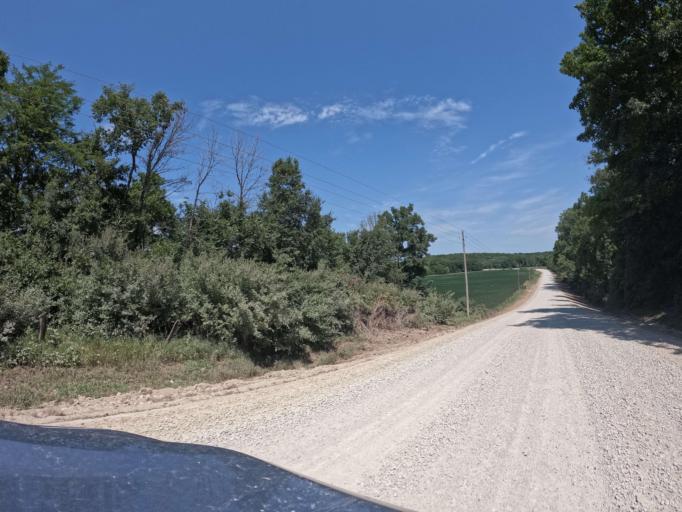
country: US
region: Iowa
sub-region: Henry County
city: Mount Pleasant
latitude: 40.9047
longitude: -91.6774
